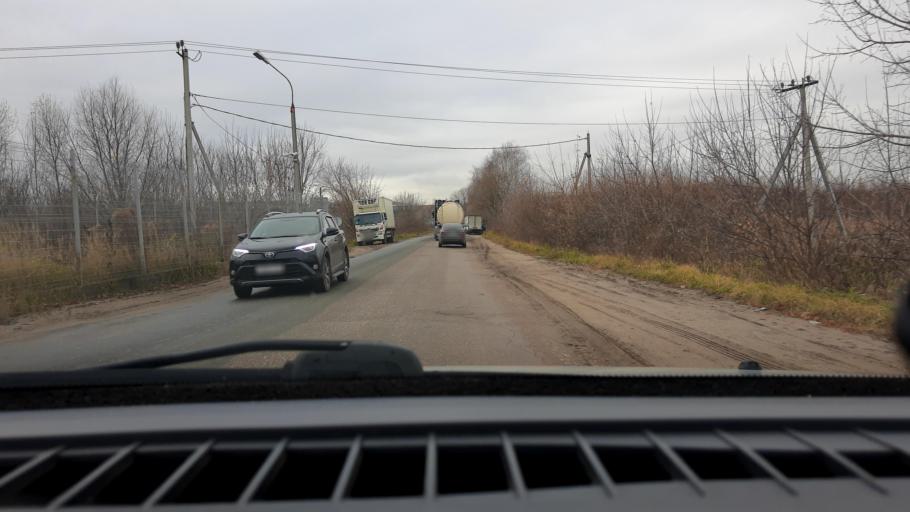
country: RU
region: Nizjnij Novgorod
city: Kstovo
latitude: 56.1934
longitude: 44.1364
